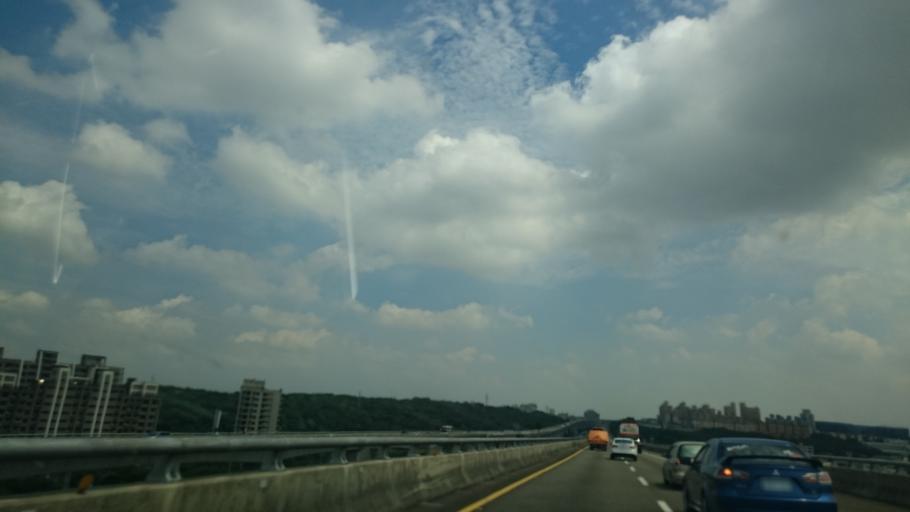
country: TW
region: Taiwan
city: Daxi
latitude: 24.9090
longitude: 121.1648
